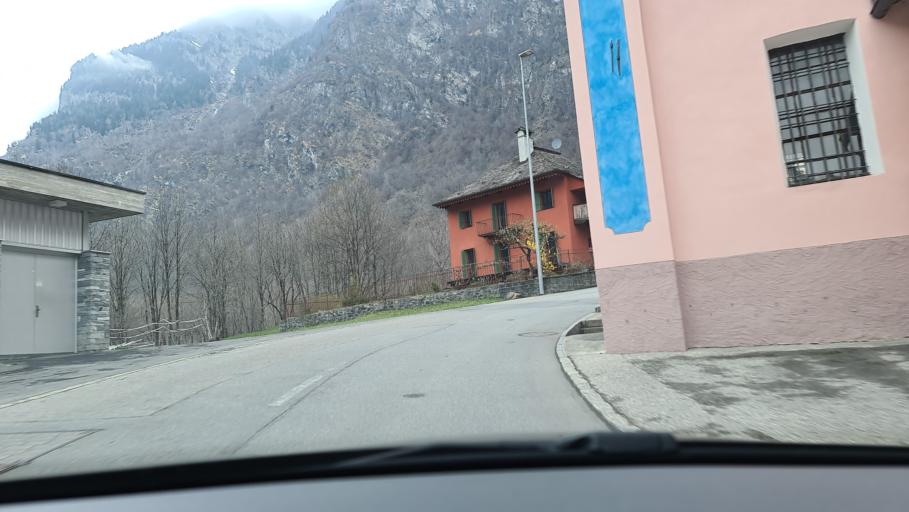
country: CH
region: Ticino
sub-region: Vallemaggia District
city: Cevio
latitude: 46.4056
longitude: 8.6480
